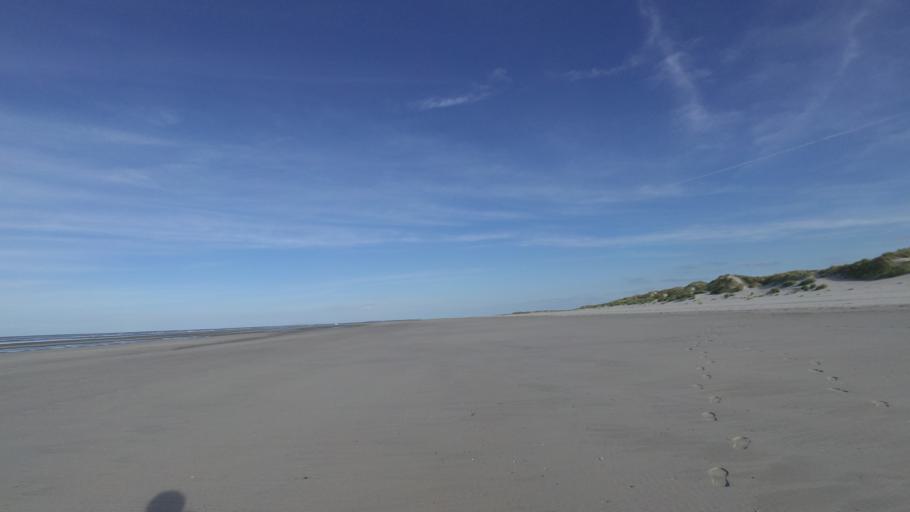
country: NL
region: Friesland
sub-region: Gemeente Dongeradeel
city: Ternaard
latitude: 53.4682
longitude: 5.9161
